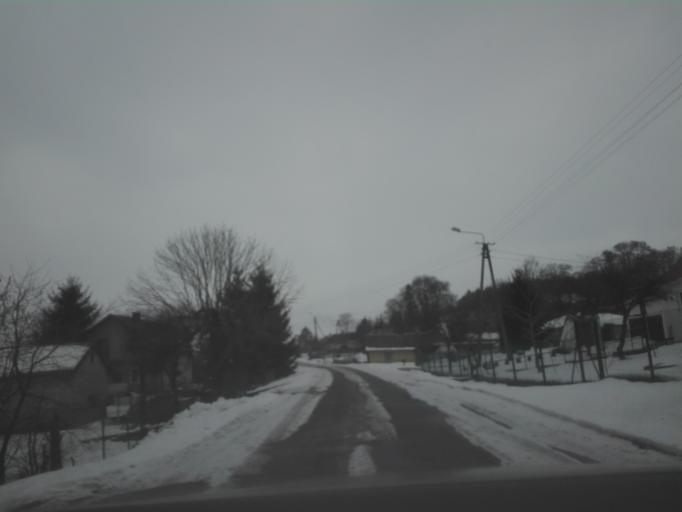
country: PL
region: Lublin Voivodeship
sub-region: Powiat hrubieszowski
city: Horodlo
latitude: 50.8458
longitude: 24.0278
